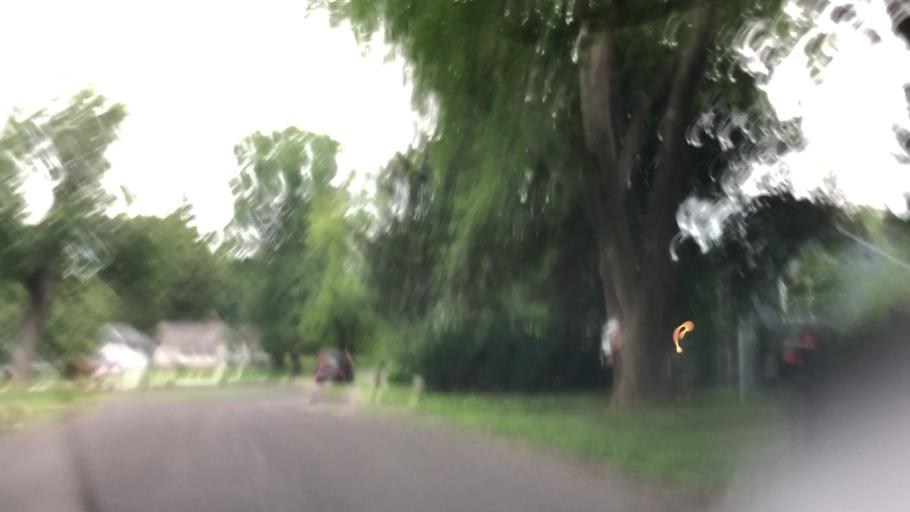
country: US
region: Ohio
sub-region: Stark County
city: North Canton
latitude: 40.8511
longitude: -81.3913
